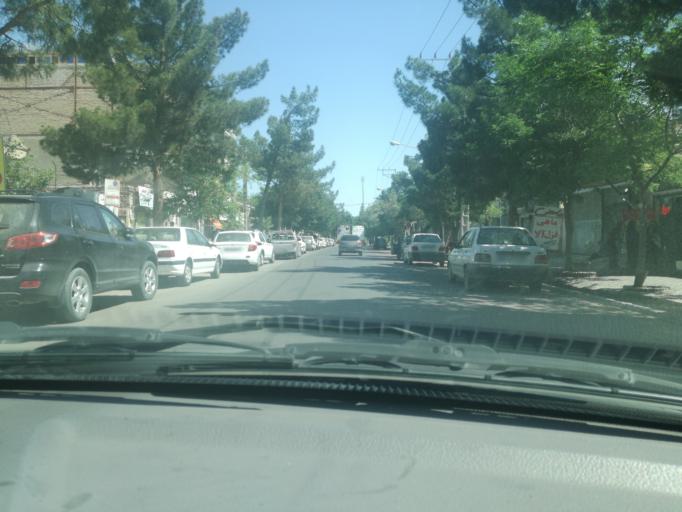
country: IR
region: Razavi Khorasan
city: Sarakhs
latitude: 36.5407
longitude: 61.1637
